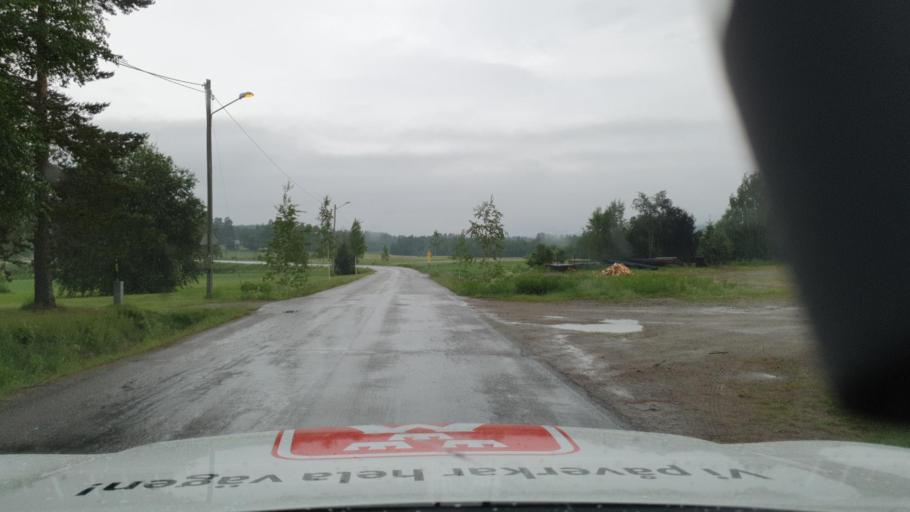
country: SE
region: Vaesterbotten
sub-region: Nordmalings Kommun
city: Nordmaling
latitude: 63.7969
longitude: 19.5088
